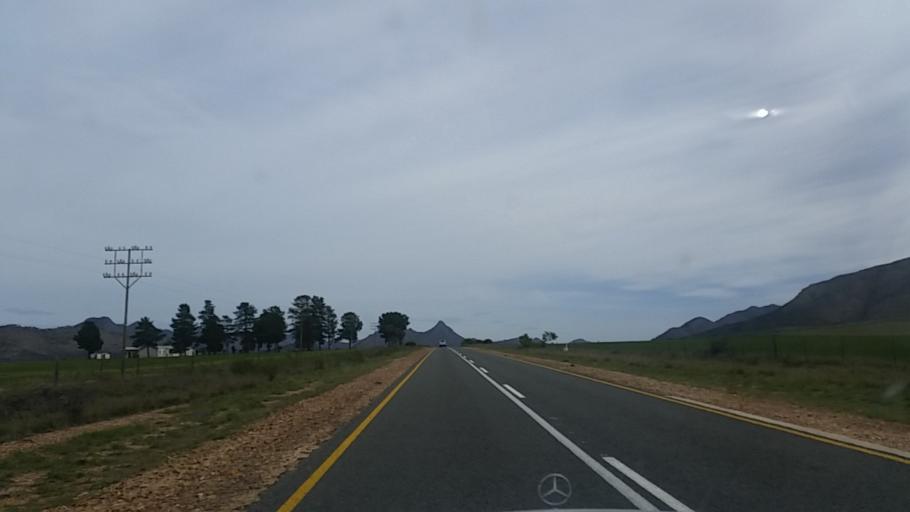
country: ZA
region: Western Cape
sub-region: Eden District Municipality
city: George
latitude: -33.8191
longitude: 22.4996
